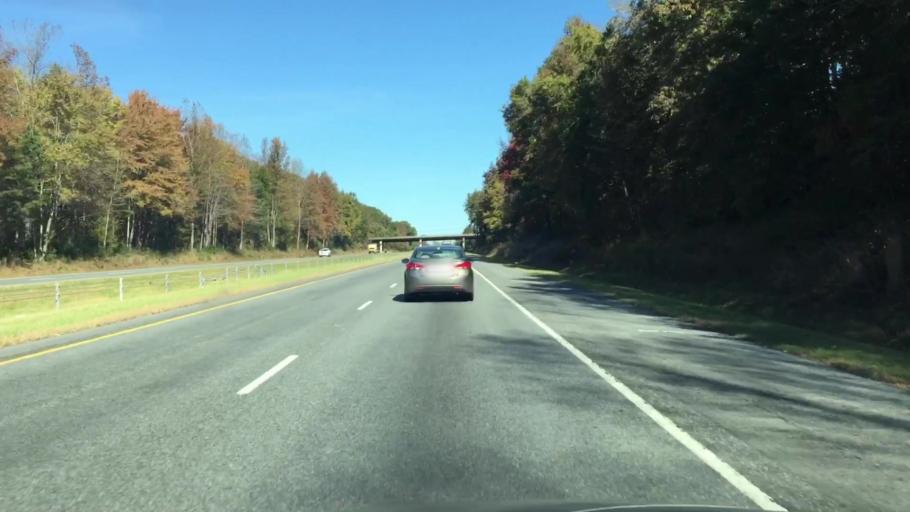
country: US
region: North Carolina
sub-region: Rockingham County
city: Reidsville
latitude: 36.2836
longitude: -79.6403
